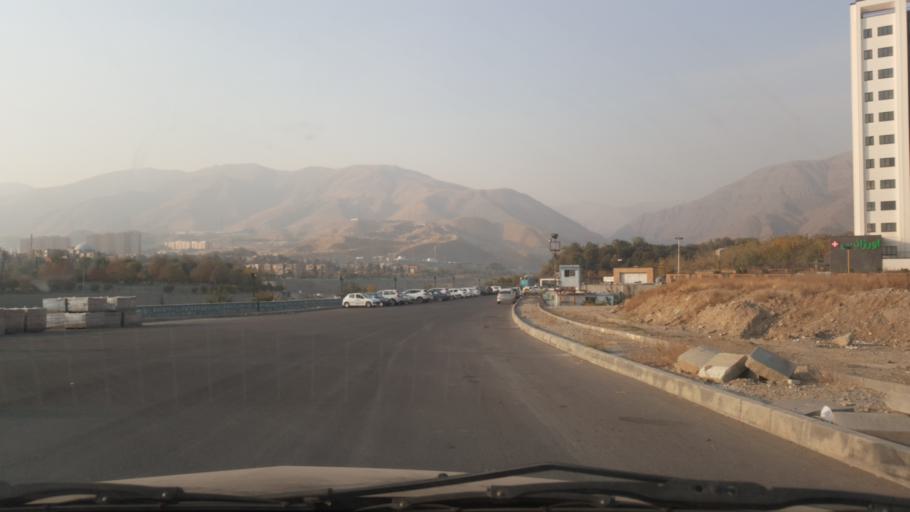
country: IR
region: Tehran
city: Tajrish
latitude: 35.7558
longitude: 51.2699
